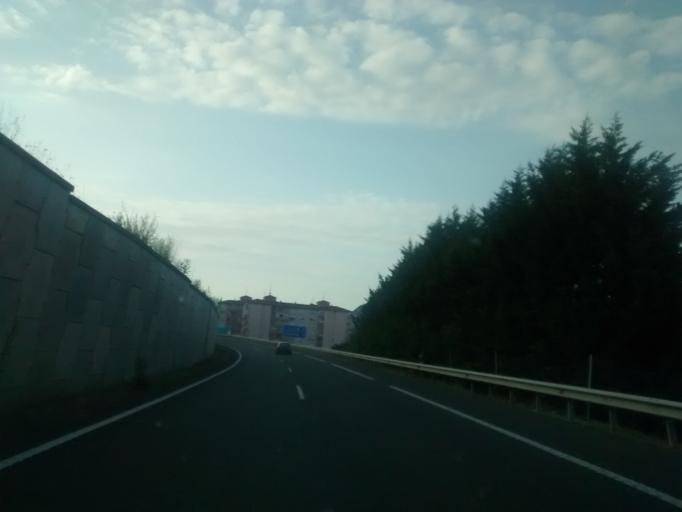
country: ES
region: Cantabria
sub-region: Provincia de Cantabria
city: Los Corrales de Buelna
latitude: 43.2586
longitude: -4.0720
